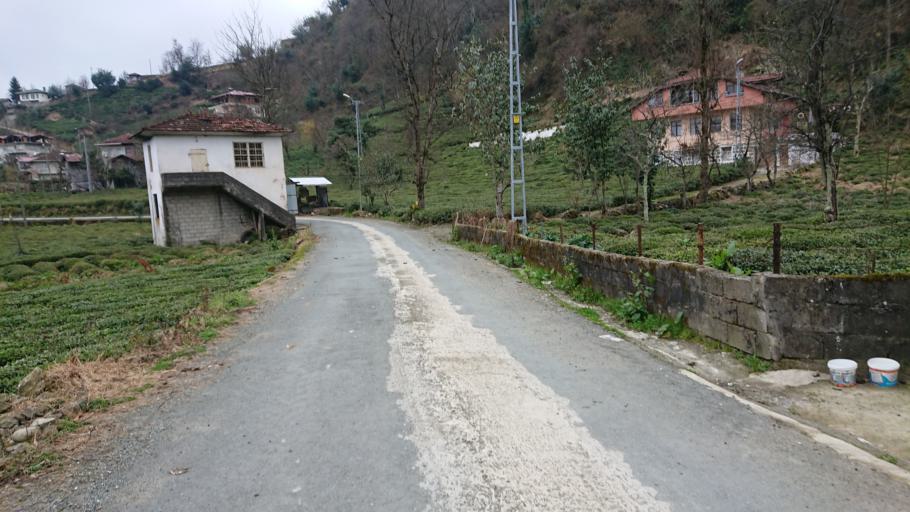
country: TR
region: Rize
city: Rize
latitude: 40.9815
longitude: 40.4952
